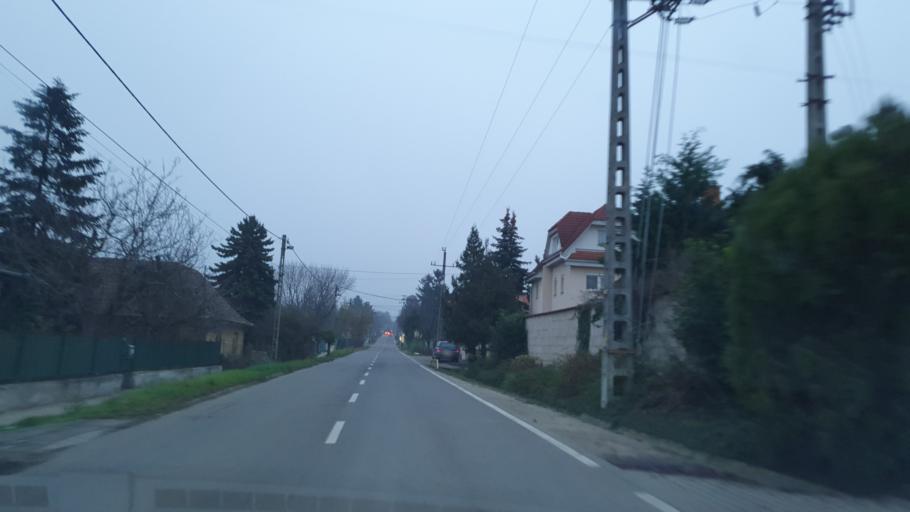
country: HU
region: Pest
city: Csomor
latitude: 47.5443
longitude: 19.2203
